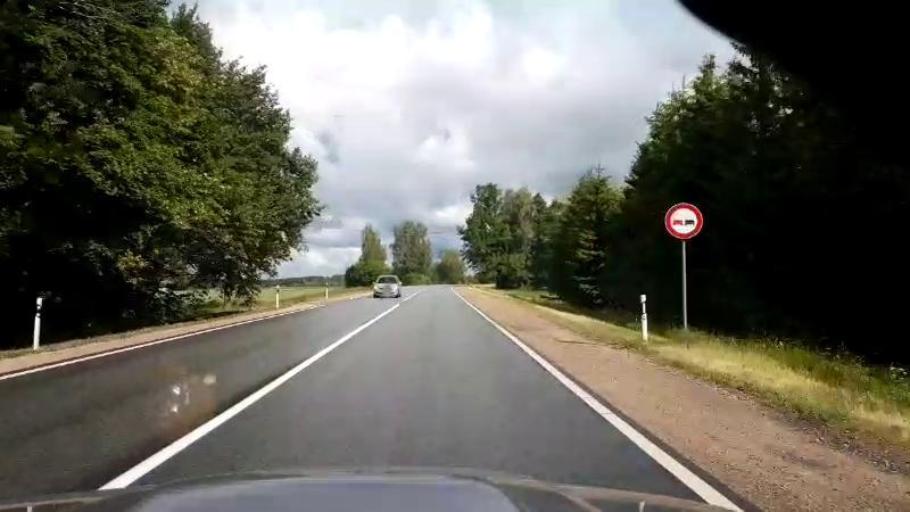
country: LV
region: Lecava
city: Iecava
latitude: 56.5281
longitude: 24.1706
